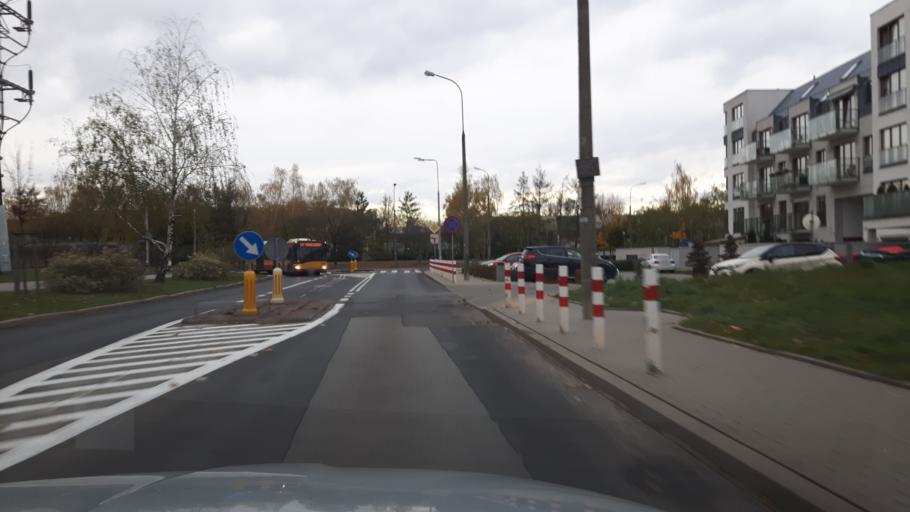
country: PL
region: Masovian Voivodeship
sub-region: Warszawa
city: Ursynow
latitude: 52.1595
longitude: 21.0543
